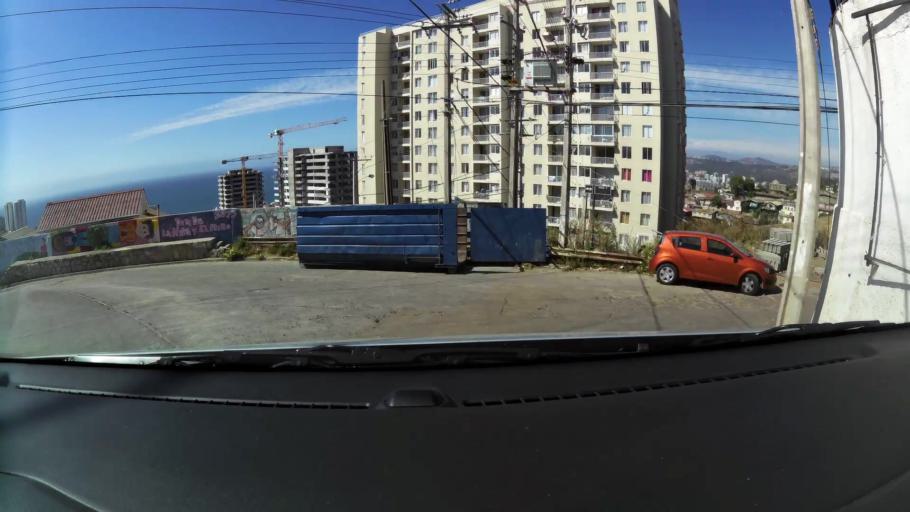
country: CL
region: Valparaiso
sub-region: Provincia de Valparaiso
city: Vina del Mar
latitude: -33.0361
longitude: -71.5737
